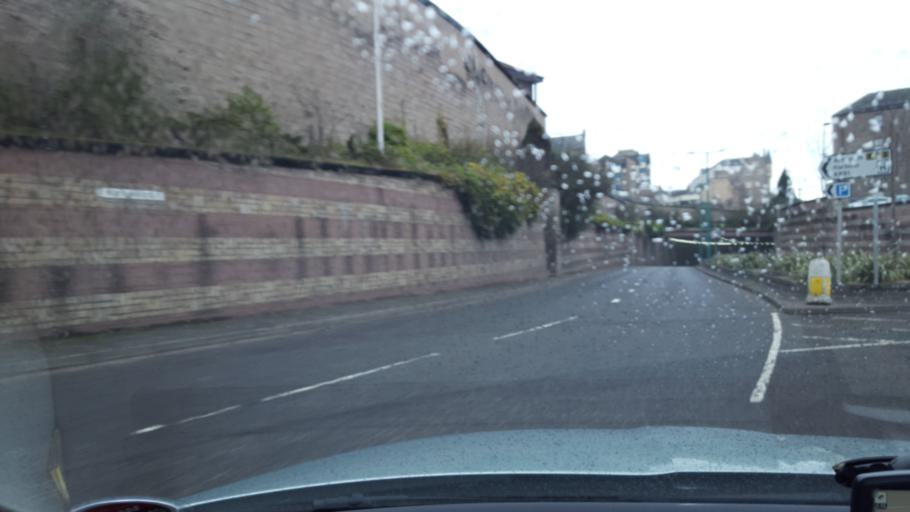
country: GB
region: Scotland
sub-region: Dundee City
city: Dundee
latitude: 56.4645
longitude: -2.9731
